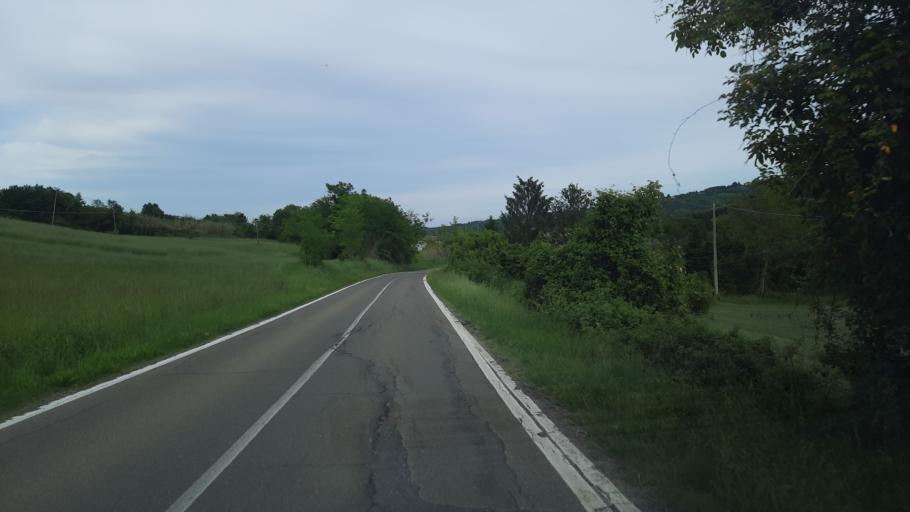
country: IT
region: Piedmont
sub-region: Provincia di Alessandria
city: Coniolo Bricco
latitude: 45.1422
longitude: 8.3808
